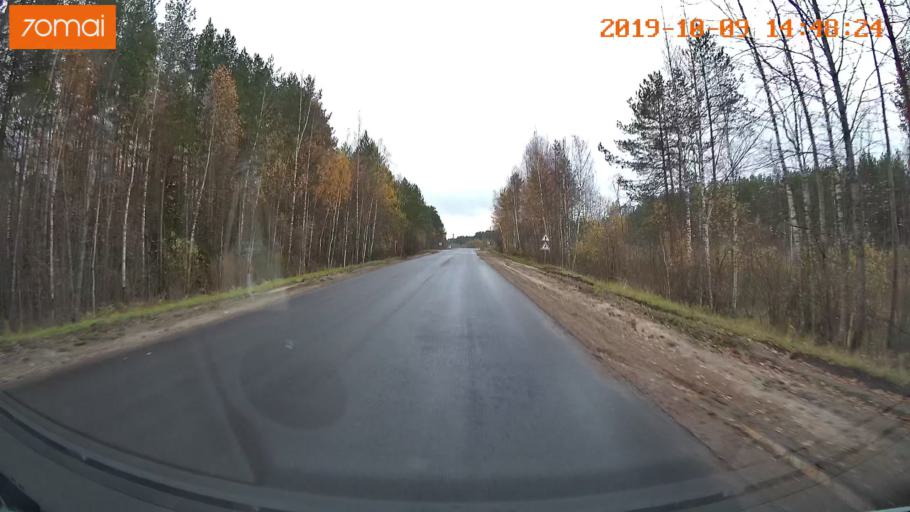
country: RU
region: Kostroma
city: Chistyye Bory
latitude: 58.4061
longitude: 41.5752
